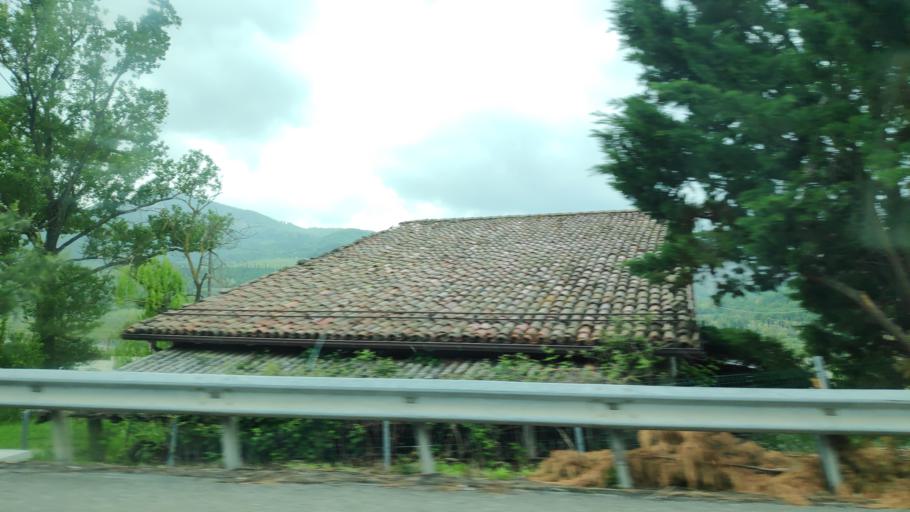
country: IT
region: Emilia-Romagna
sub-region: Provincia di Parma
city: Varano De' Melegari
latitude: 44.6494
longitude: 10.0486
